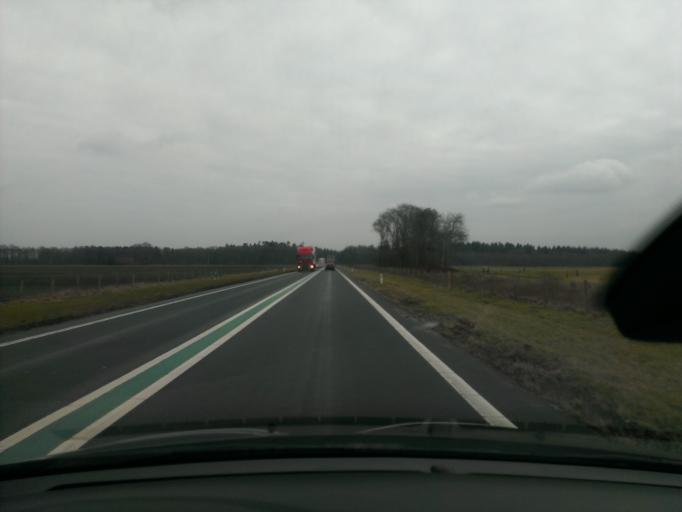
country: NL
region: Overijssel
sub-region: Gemeente Twenterand
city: Magele
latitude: 52.5602
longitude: 6.5124
